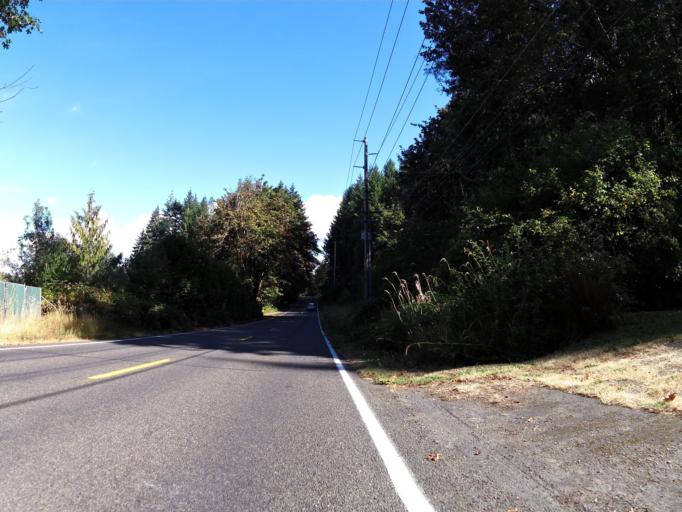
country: US
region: Washington
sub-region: Thurston County
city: Olympia
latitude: 47.0570
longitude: -123.0104
